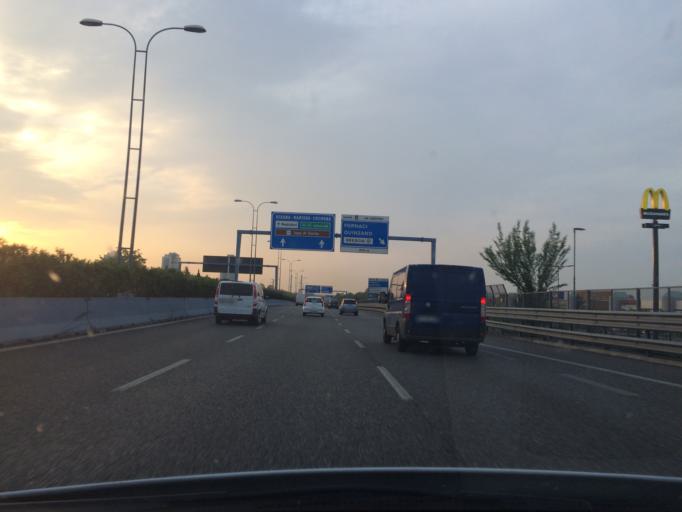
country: IT
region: Lombardy
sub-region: Provincia di Brescia
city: Roncadelle
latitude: 45.5226
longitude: 10.1833
